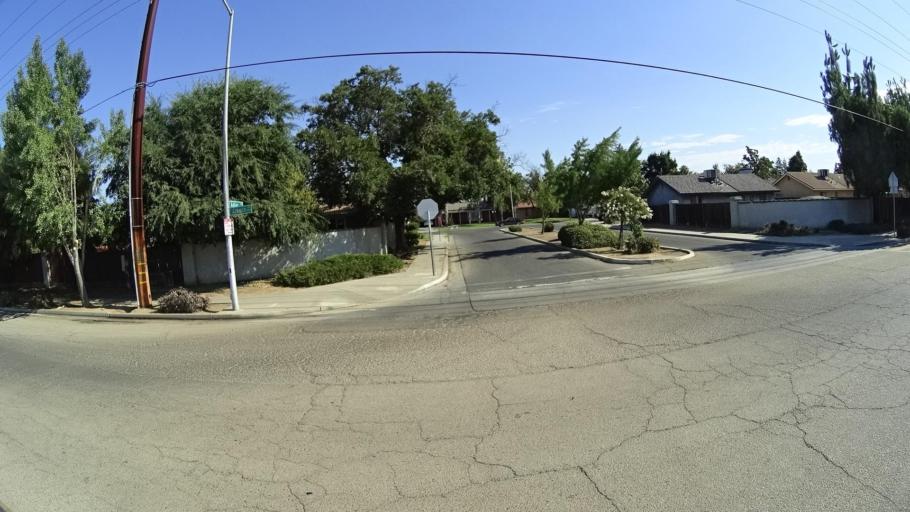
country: US
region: California
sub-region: Fresno County
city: Sunnyside
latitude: 36.7146
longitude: -119.7255
